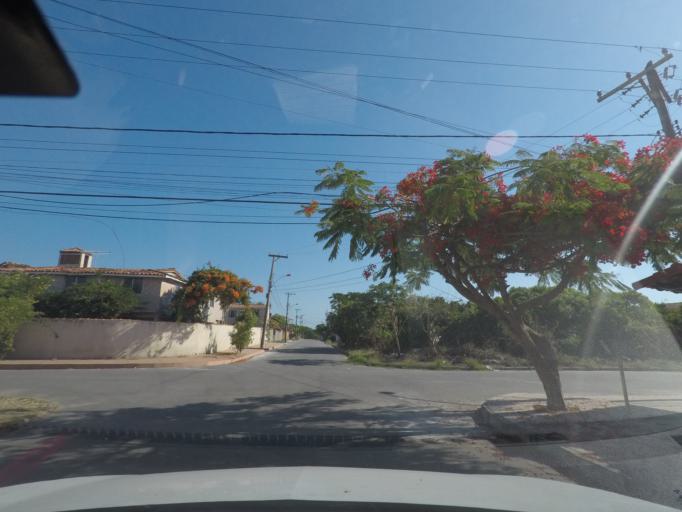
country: BR
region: Rio de Janeiro
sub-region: Marica
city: Marica
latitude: -22.9694
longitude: -42.9190
